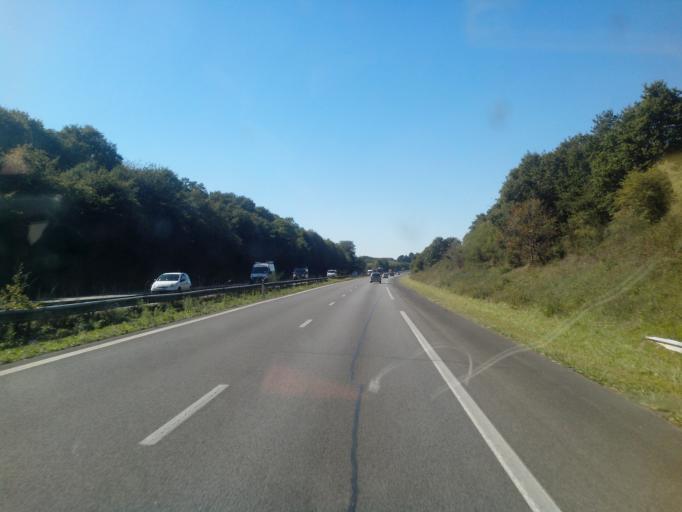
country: FR
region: Pays de la Loire
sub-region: Departement de la Loire-Atlantique
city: Sautron
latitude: 47.2537
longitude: -1.6690
